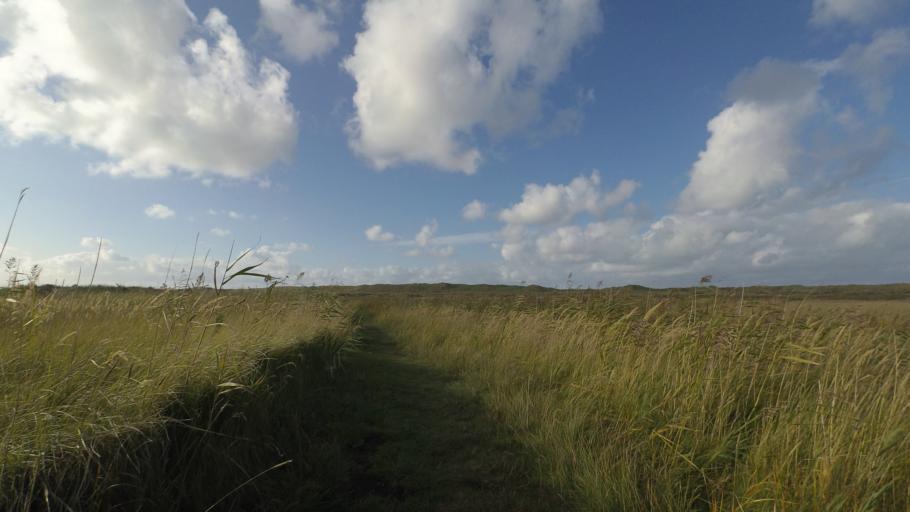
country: NL
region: Friesland
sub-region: Gemeente Dongeradeel
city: Ternaard
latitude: 53.4631
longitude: 5.9163
